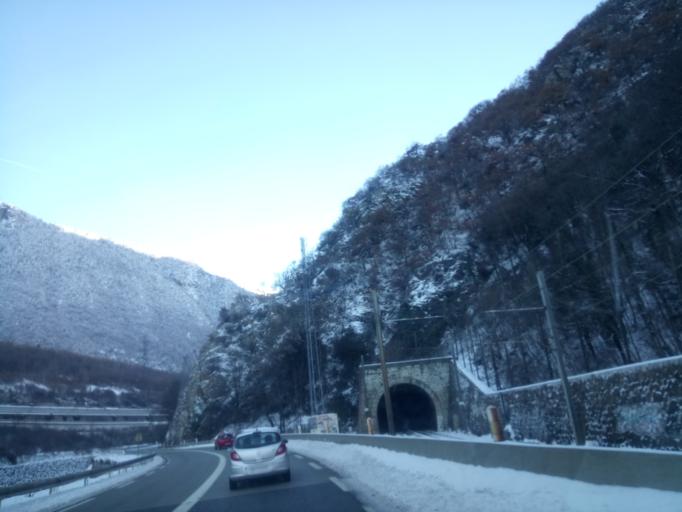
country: FR
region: Rhone-Alpes
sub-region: Departement de la Savoie
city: La Chambre
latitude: 45.3198
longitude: 6.3242
